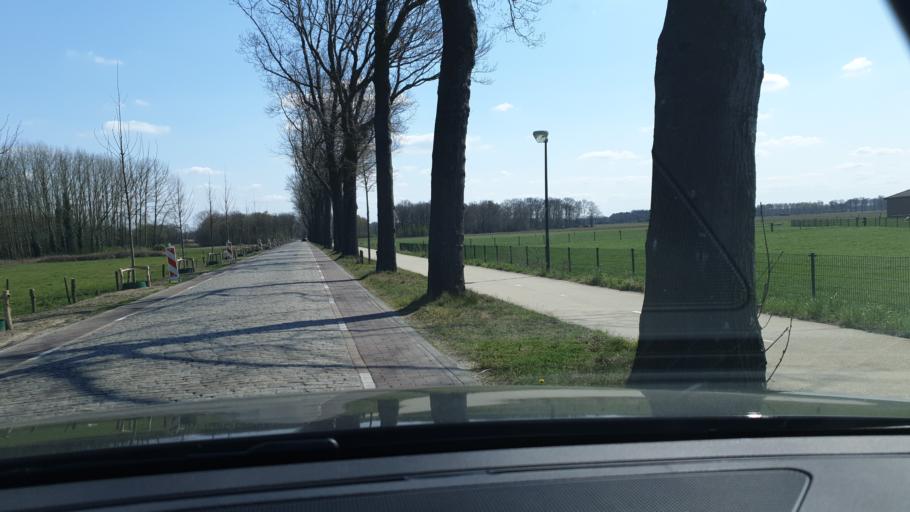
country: NL
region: North Brabant
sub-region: Gemeente Bladel en Netersel
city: Bladel
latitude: 51.4018
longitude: 5.2226
